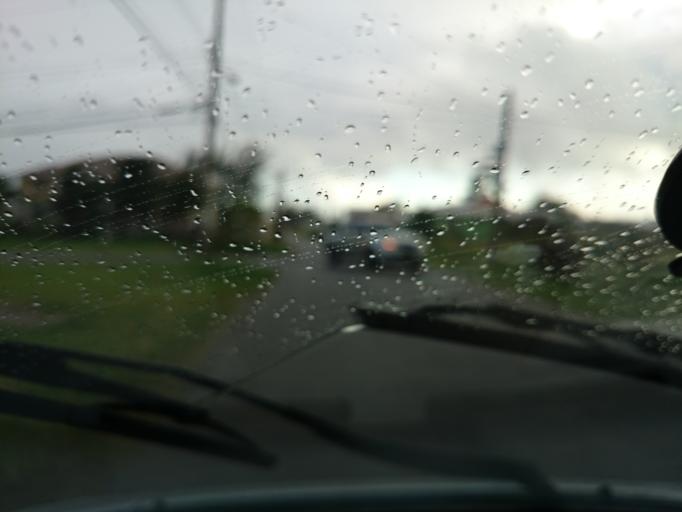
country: BB
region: Christ Church
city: Oistins
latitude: 13.0553
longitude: -59.5110
